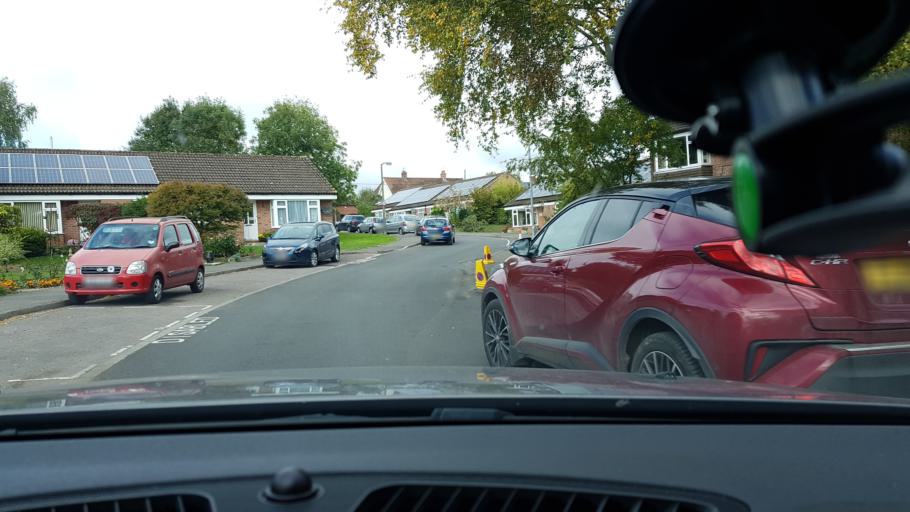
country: GB
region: England
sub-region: Wiltshire
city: Great Bedwyn
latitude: 51.3808
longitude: -1.5981
